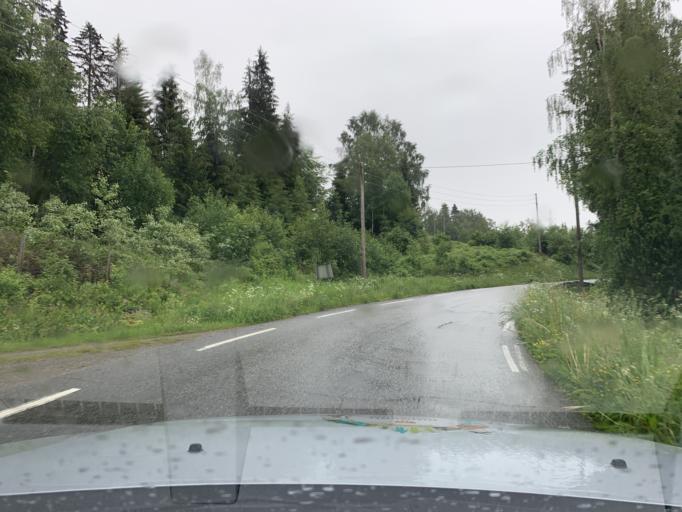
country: NO
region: Oppland
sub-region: Oyer
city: Tretten
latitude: 61.3944
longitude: 10.2401
